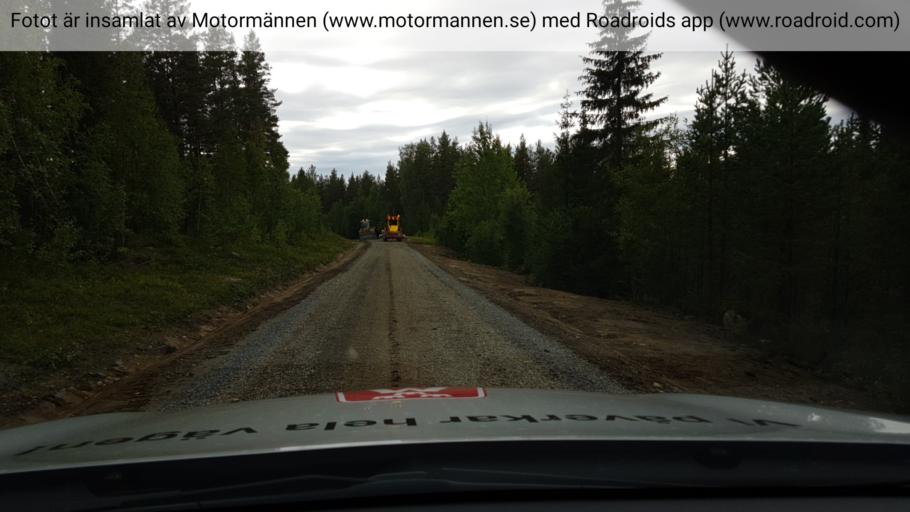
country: SE
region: Jaemtland
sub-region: Ragunda Kommun
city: Hammarstrand
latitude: 62.8704
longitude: 16.0553
